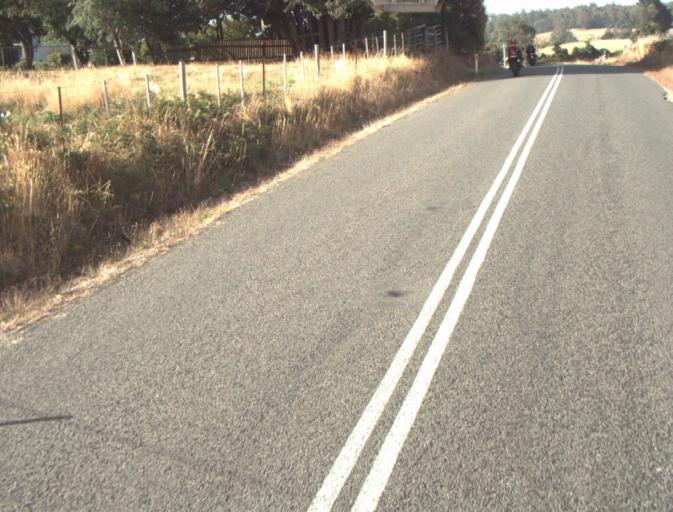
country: AU
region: Tasmania
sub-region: Launceston
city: Mayfield
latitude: -41.1878
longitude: 147.2219
